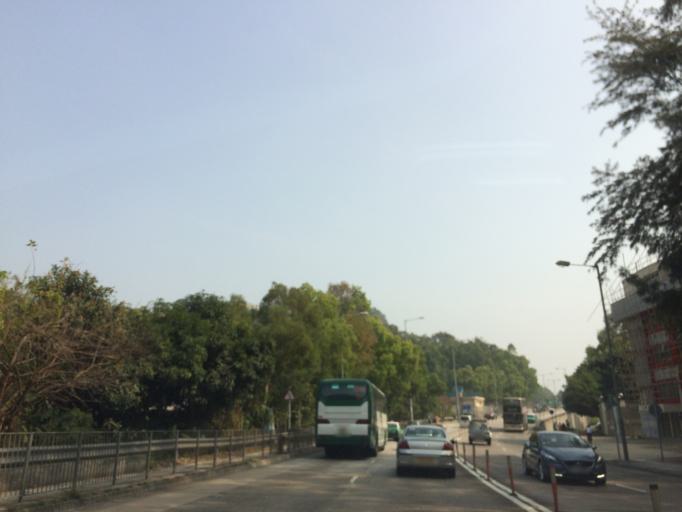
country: HK
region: Tai Po
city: Tai Po
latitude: 22.4623
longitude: 114.1900
